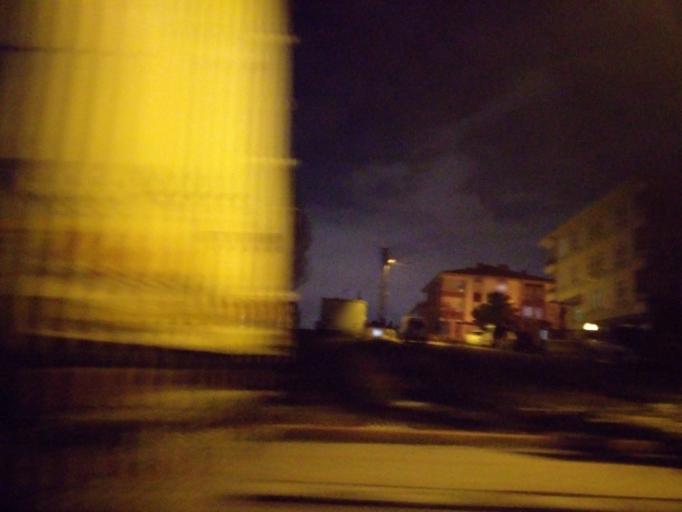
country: TR
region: Ankara
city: Ankara
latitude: 39.9771
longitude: 32.8229
